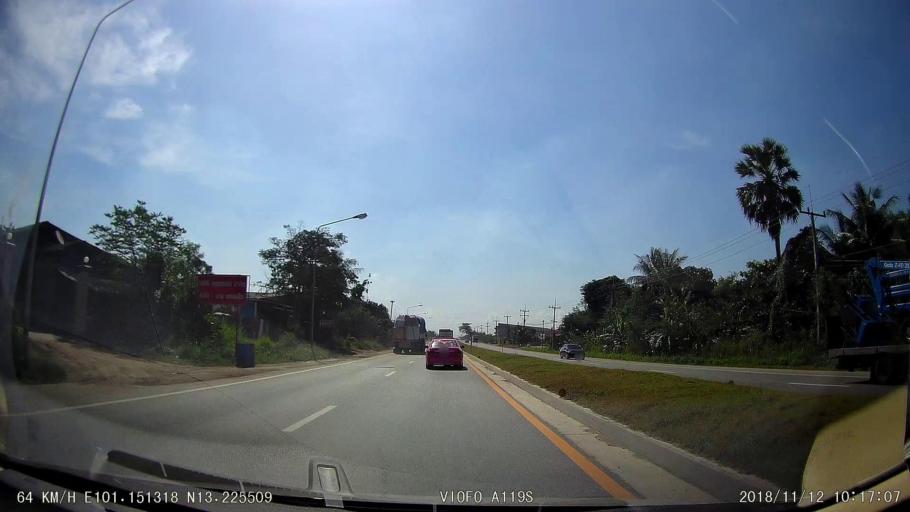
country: TH
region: Chon Buri
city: Ban Bueng
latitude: 13.2254
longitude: 101.1514
